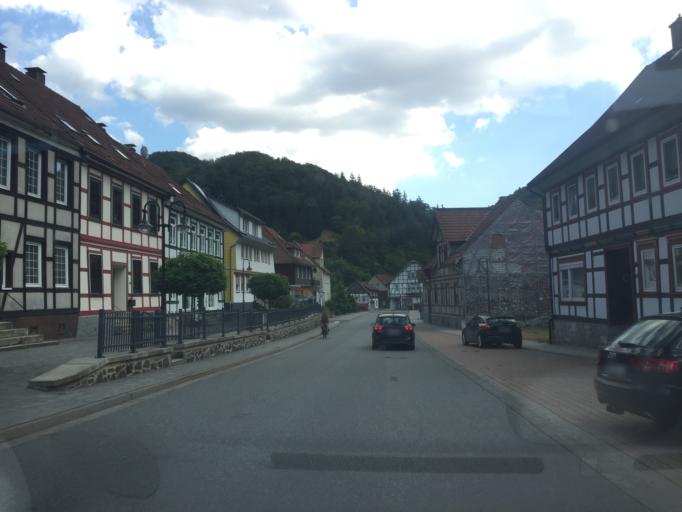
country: DE
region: Lower Saxony
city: Zorge
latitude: 51.6354
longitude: 10.6334
